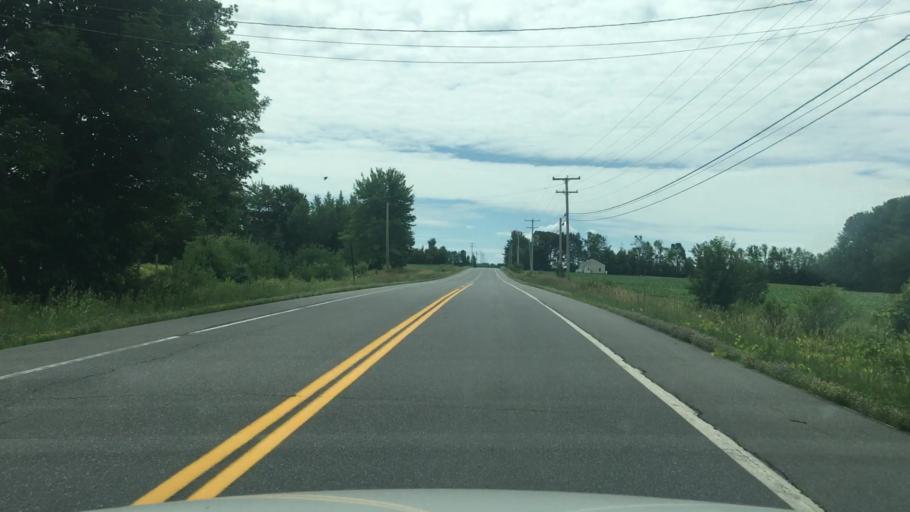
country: US
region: Maine
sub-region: Waldo County
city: Troy
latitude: 44.5597
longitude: -69.2711
